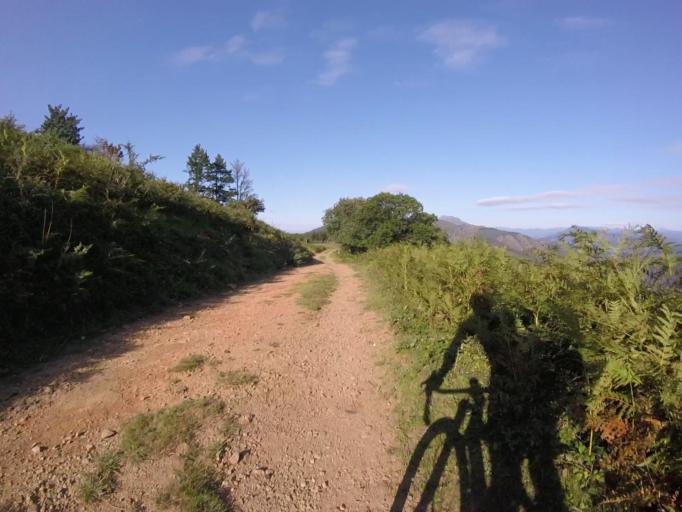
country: ES
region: Basque Country
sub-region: Provincia de Guipuzcoa
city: Irun
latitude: 43.3000
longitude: -1.7470
